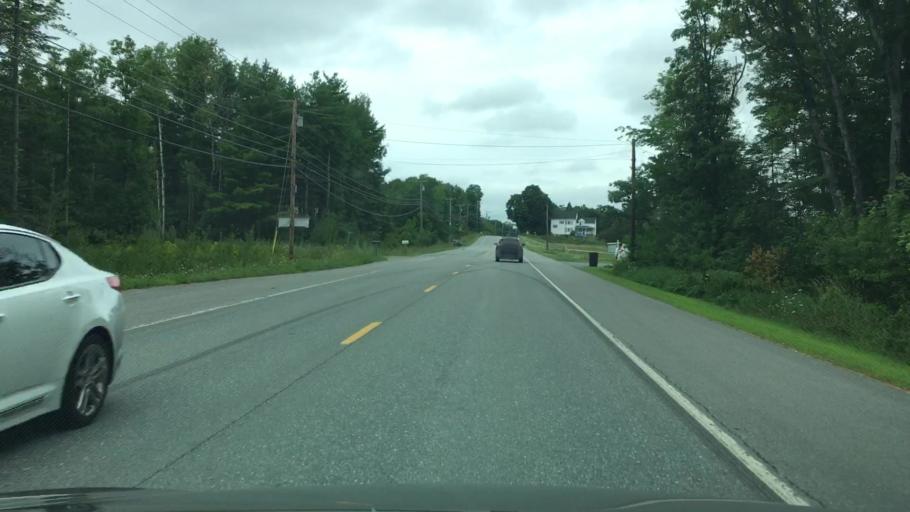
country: US
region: Maine
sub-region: Penobscot County
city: Orrington
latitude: 44.7086
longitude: -68.8247
